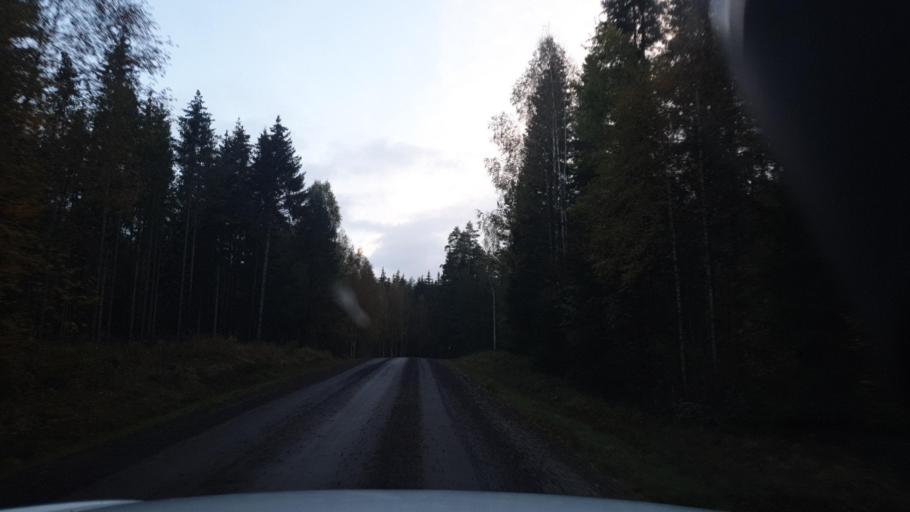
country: SE
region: Vaermland
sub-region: Arvika Kommun
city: Arvika
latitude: 59.7519
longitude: 12.5179
